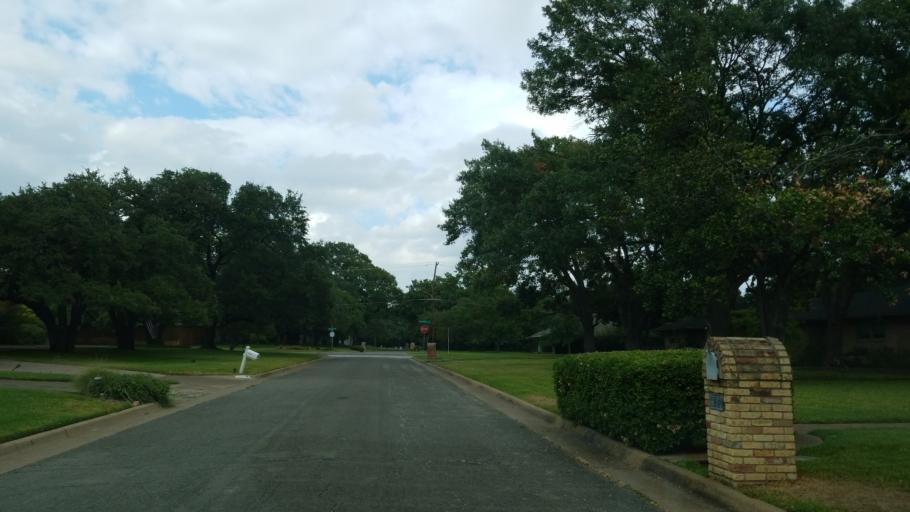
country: US
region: Texas
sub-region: Dallas County
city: Richardson
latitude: 32.9353
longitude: -96.7795
